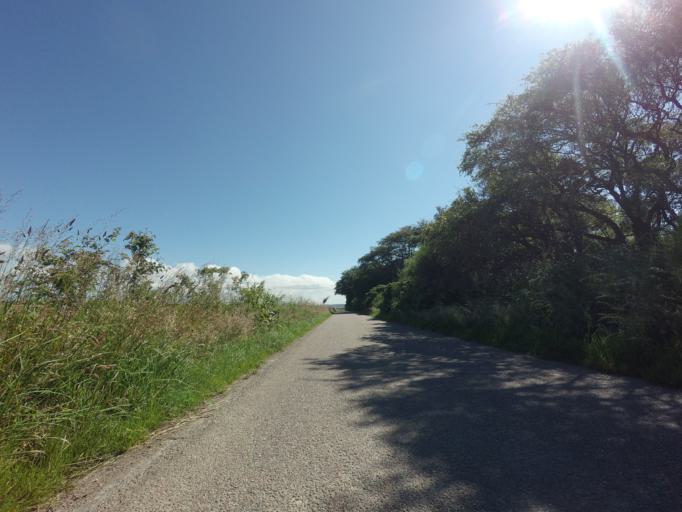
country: GB
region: Scotland
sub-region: Aberdeenshire
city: Macduff
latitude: 57.6489
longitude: -2.5042
